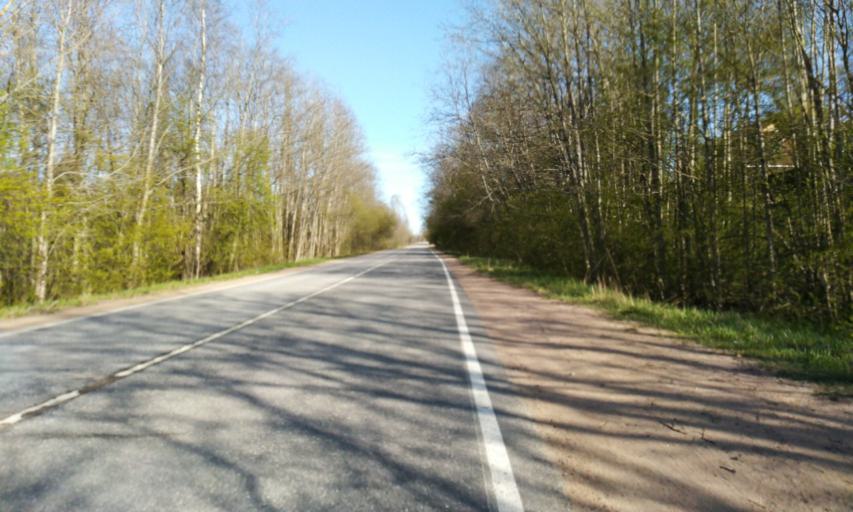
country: RU
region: Leningrad
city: Leskolovo
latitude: 60.3254
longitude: 30.4273
